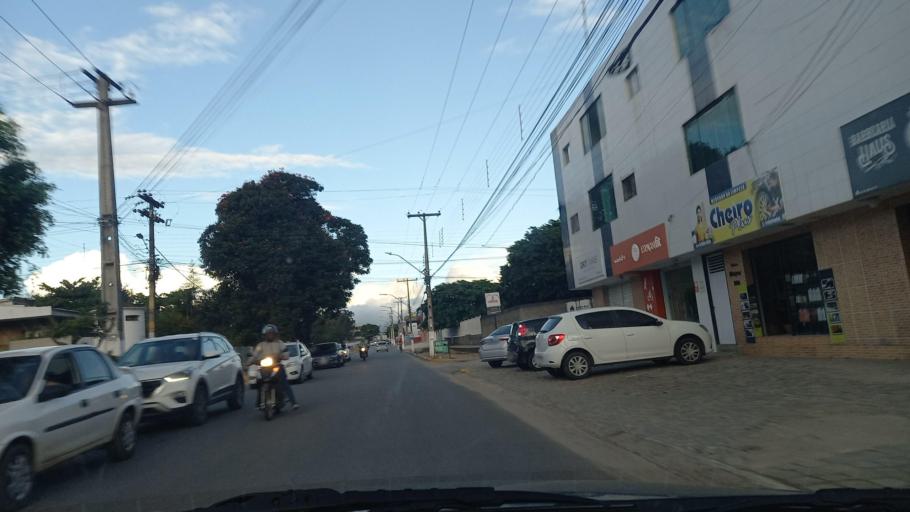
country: BR
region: Pernambuco
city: Garanhuns
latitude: -8.8835
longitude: -36.4731
